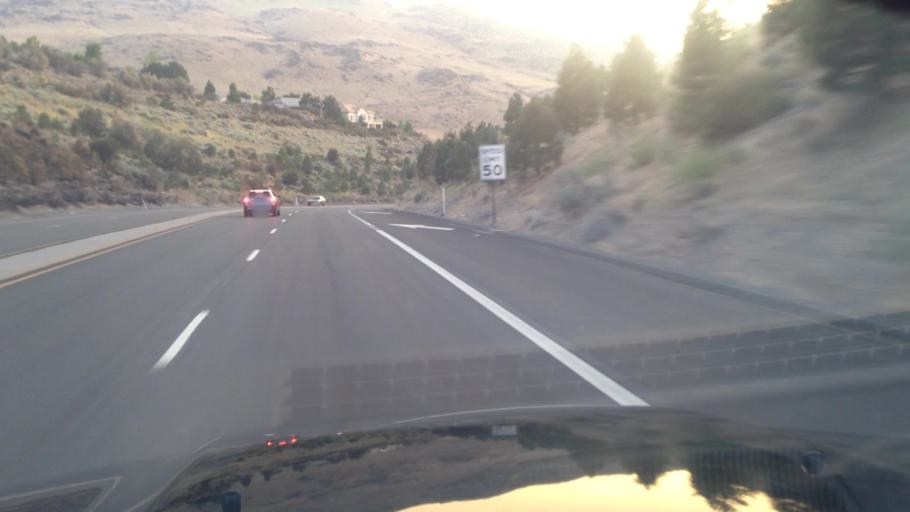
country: US
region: Nevada
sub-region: Washoe County
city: Reno
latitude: 39.4868
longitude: -119.8590
